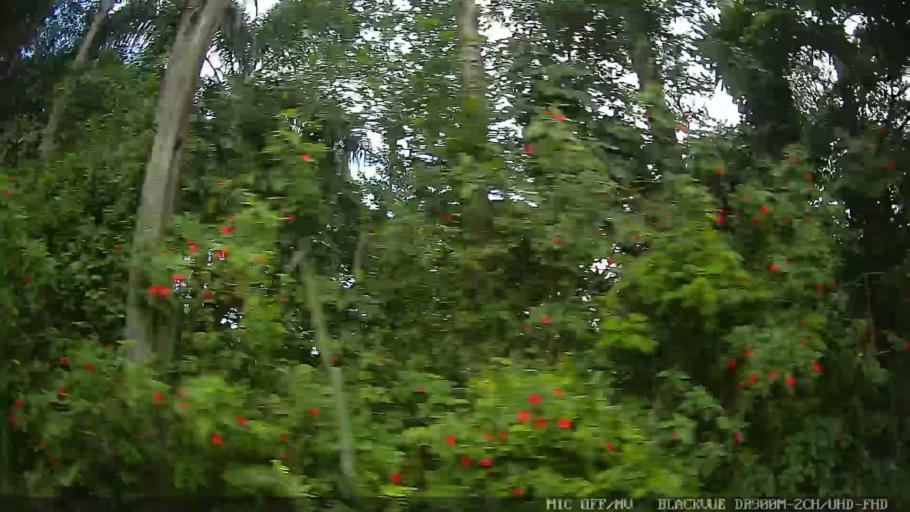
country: BR
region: Sao Paulo
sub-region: Iguape
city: Iguape
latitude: -24.6695
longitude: -47.4422
